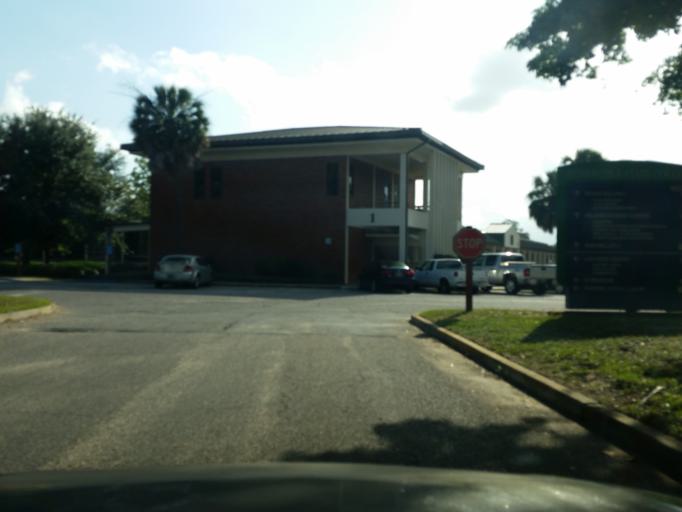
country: US
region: Florida
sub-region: Escambia County
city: Ferry Pass
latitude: 30.4813
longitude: -87.1997
